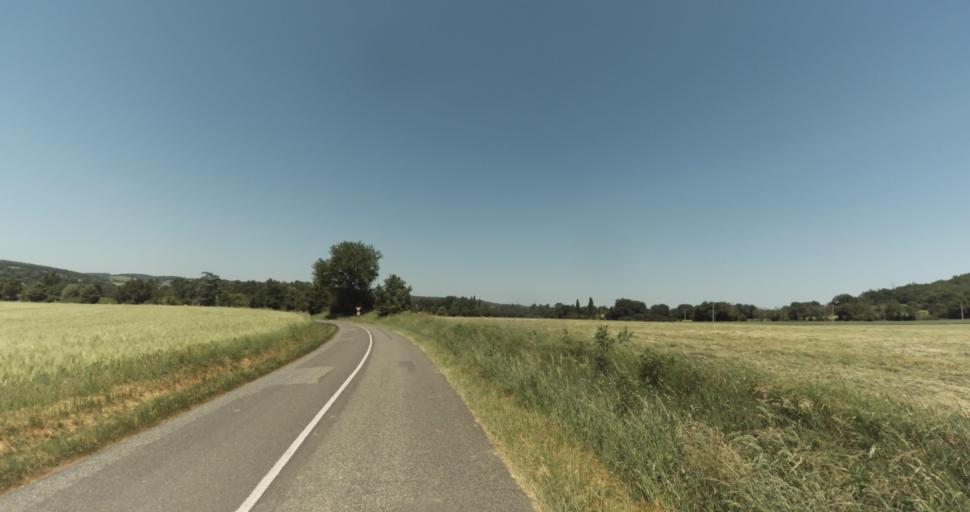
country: FR
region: Midi-Pyrenees
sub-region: Departement de la Haute-Garonne
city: Levignac
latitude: 43.6509
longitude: 1.1758
